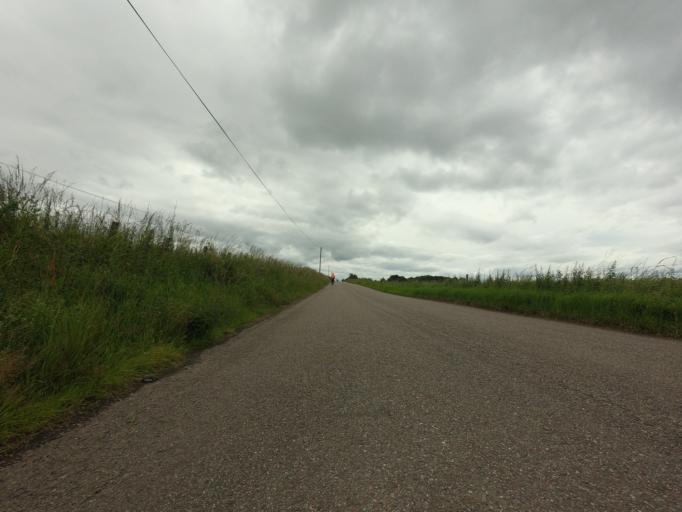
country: GB
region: Scotland
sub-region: Highland
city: Nairn
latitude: 57.5961
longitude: -3.8110
